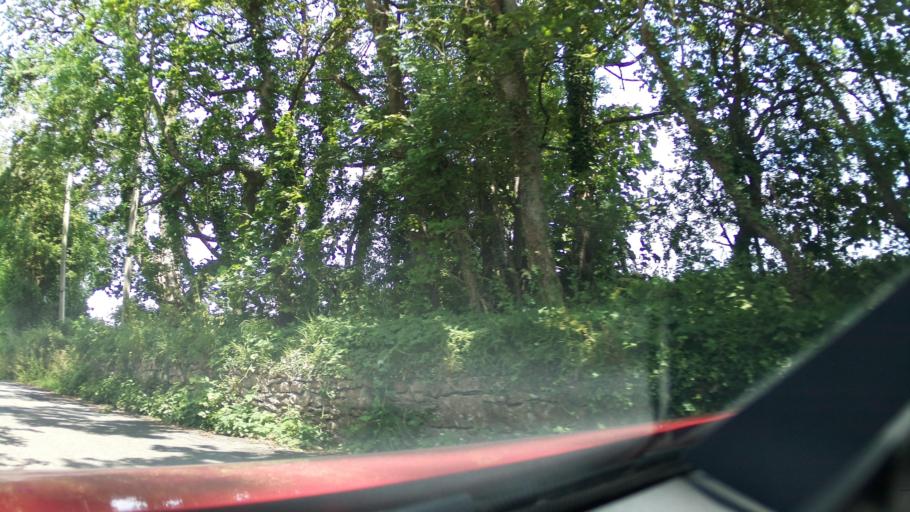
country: GB
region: Wales
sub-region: Vale of Glamorgan
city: Wick
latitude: 51.4075
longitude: -3.5315
